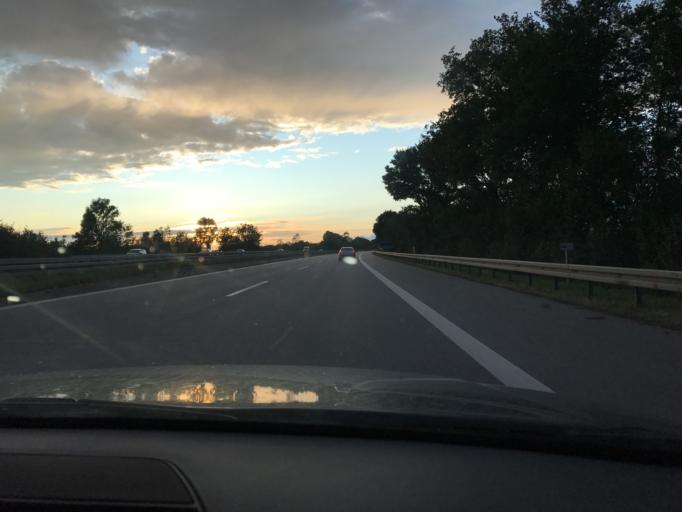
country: DE
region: Bavaria
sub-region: Upper Bavaria
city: Taufkirchen
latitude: 48.0286
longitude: 11.6266
